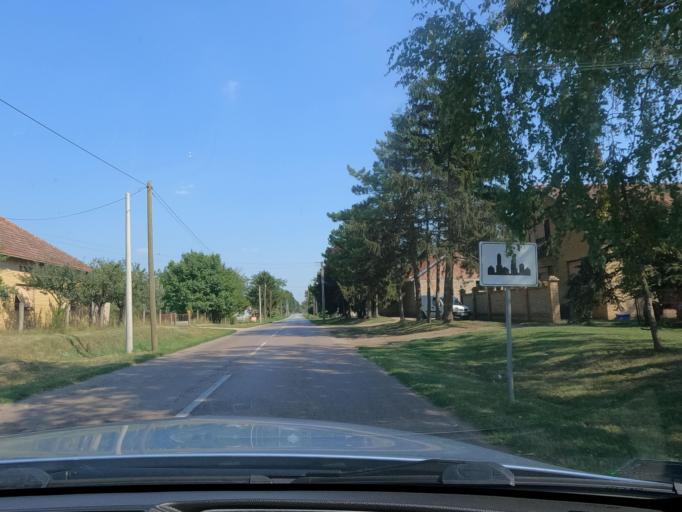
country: RS
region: Autonomna Pokrajina Vojvodina
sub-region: Severnobacki Okrug
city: Mali Igos
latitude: 45.7640
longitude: 19.7463
